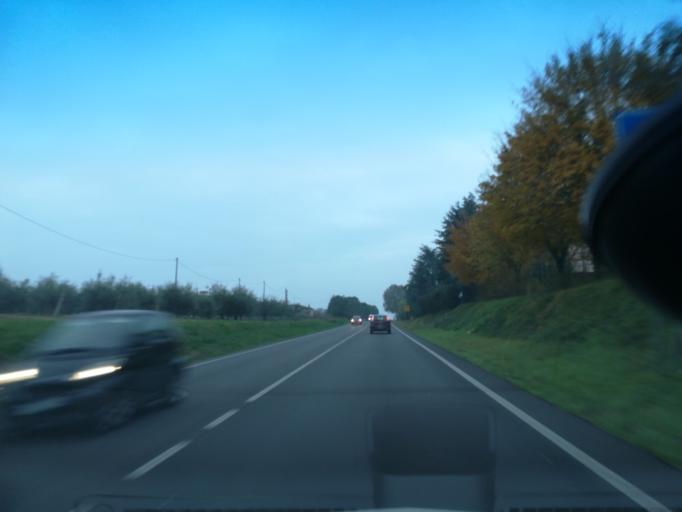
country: IT
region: Emilia-Romagna
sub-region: Provincia di Bologna
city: Imola
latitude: 44.3389
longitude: 11.7511
